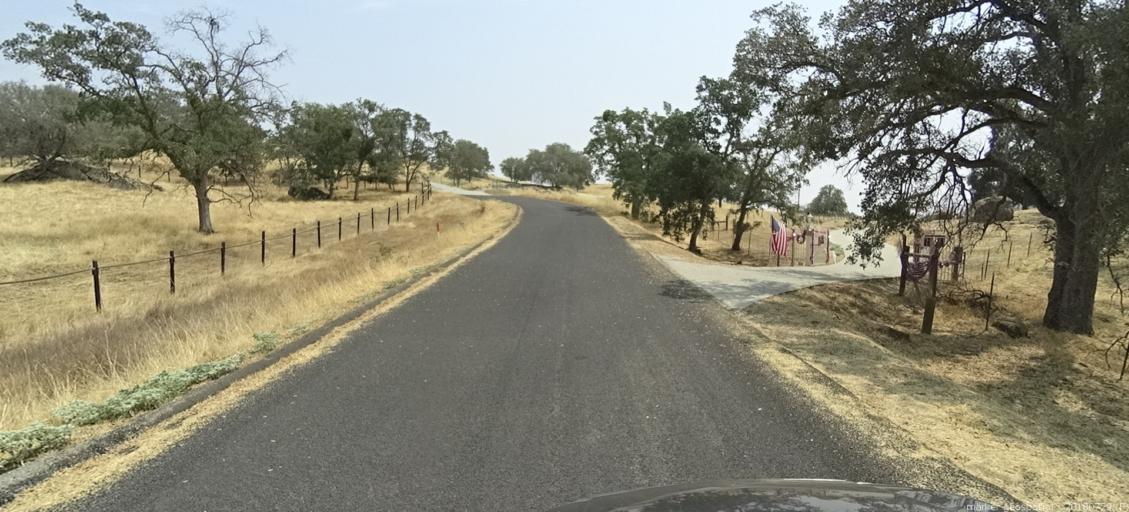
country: US
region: California
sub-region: Madera County
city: Yosemite Lakes
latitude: 37.2339
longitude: -119.9143
